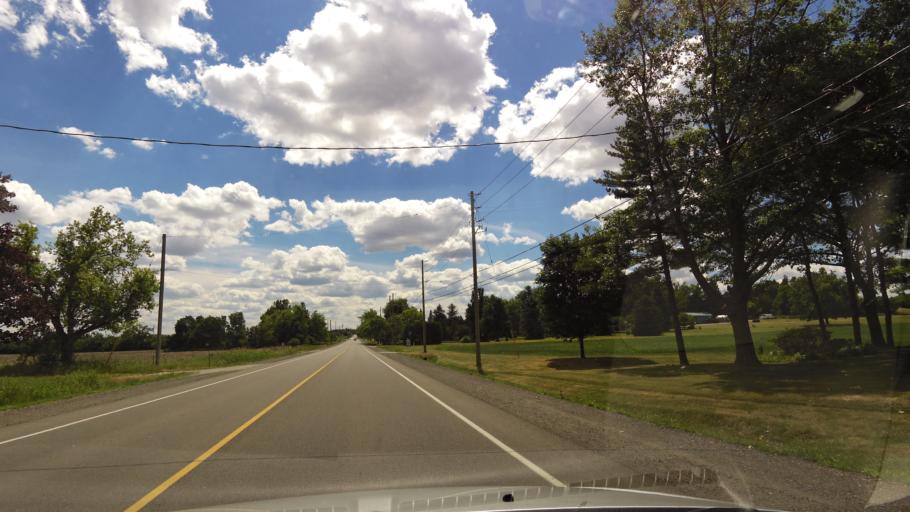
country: CA
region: Ontario
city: Brampton
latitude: 43.6305
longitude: -79.8211
